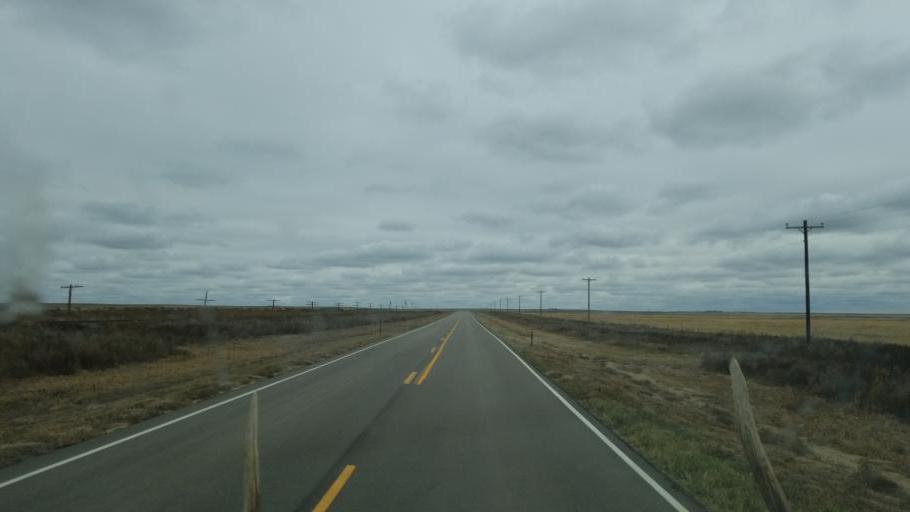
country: US
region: Colorado
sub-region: Bent County
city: Las Animas
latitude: 38.4340
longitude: -103.2407
